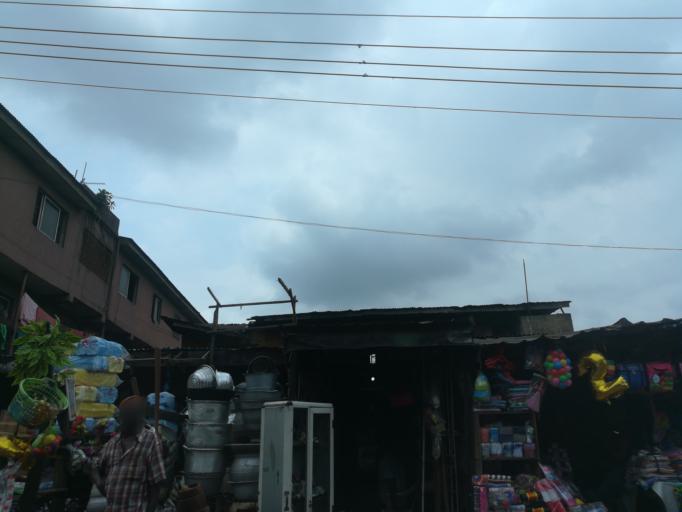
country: NG
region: Lagos
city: Agege
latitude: 6.6212
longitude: 3.3251
